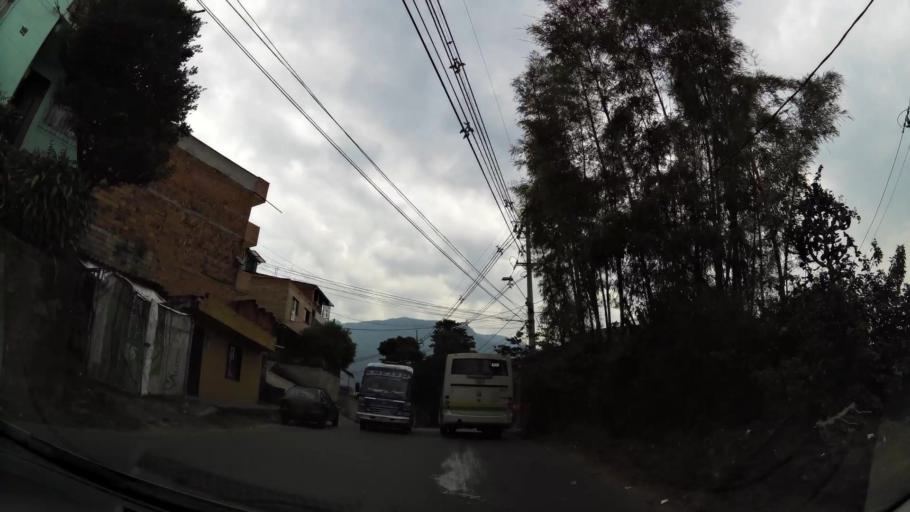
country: CO
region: Antioquia
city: Medellin
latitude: 6.2481
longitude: -75.5479
